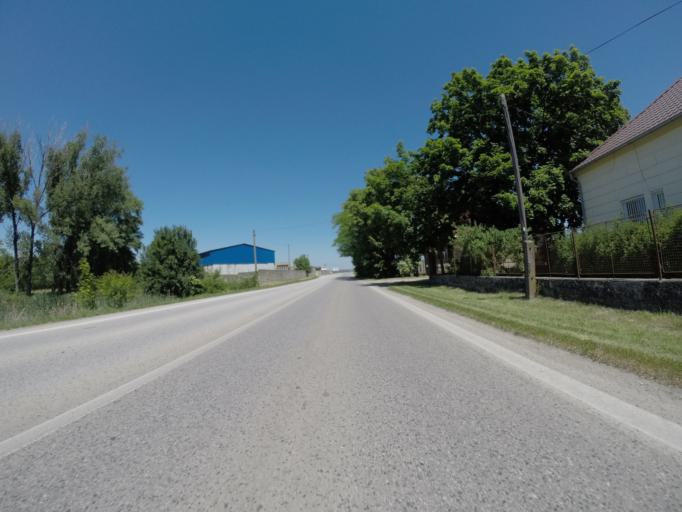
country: SK
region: Trnavsky
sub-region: Okres Galanta
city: Galanta
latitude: 48.2232
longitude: 17.7274
